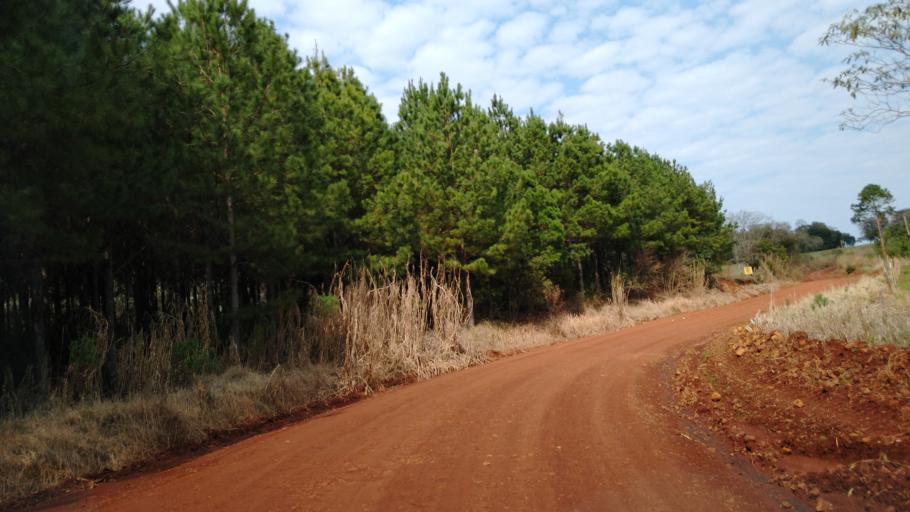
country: AR
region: Misiones
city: Capiovi
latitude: -26.9398
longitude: -55.0620
